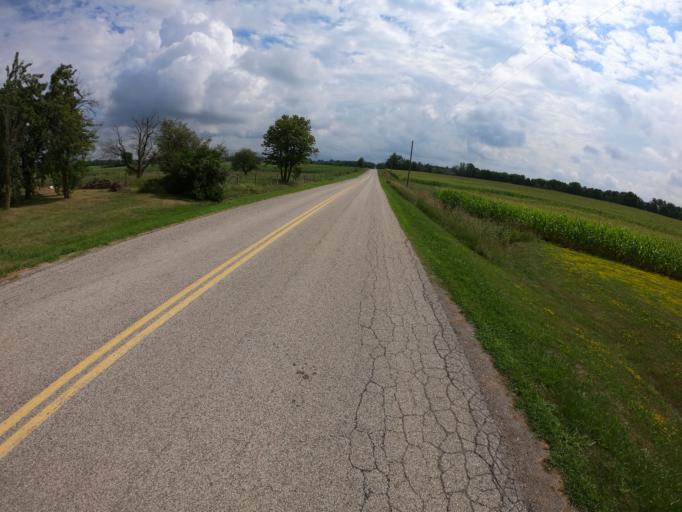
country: CA
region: Ontario
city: Waterloo
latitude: 43.4514
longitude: -80.6861
